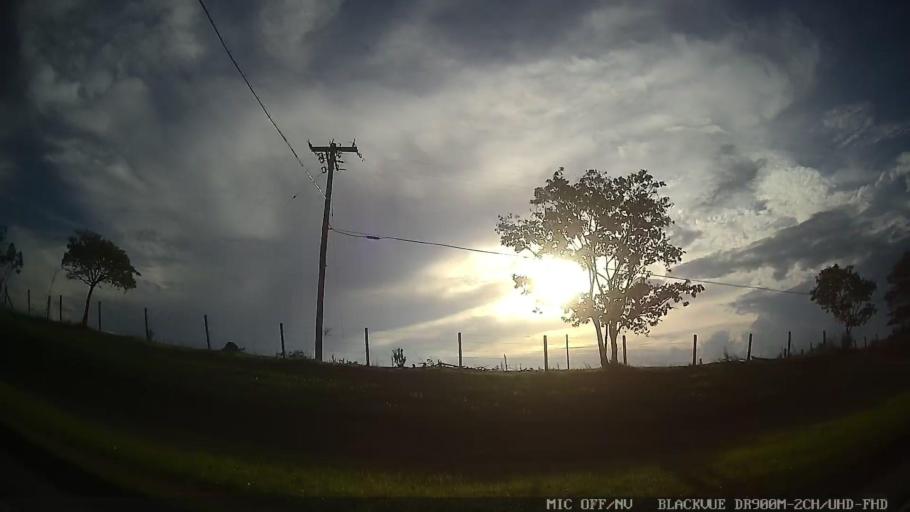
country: BR
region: Sao Paulo
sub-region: Tiete
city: Tiete
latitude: -23.1664
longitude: -47.6455
